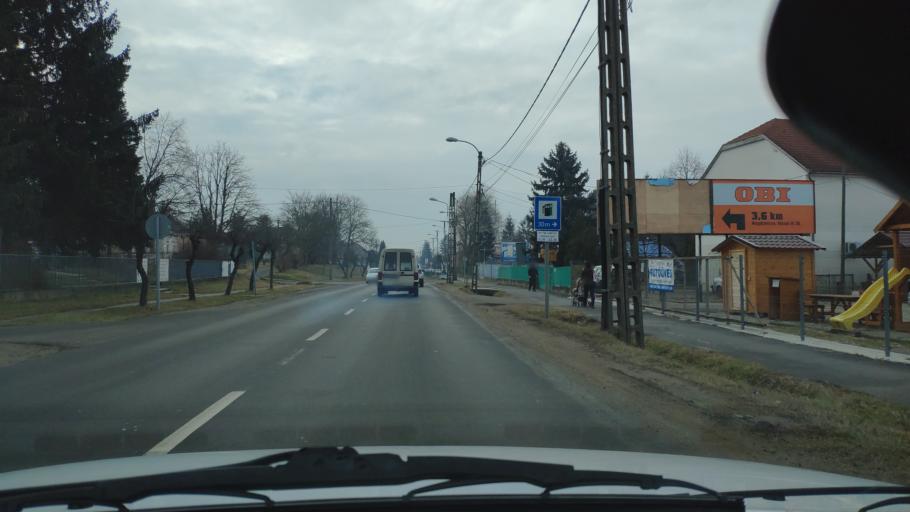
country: HU
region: Zala
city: Nagykanizsa
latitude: 46.4717
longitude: 16.9857
